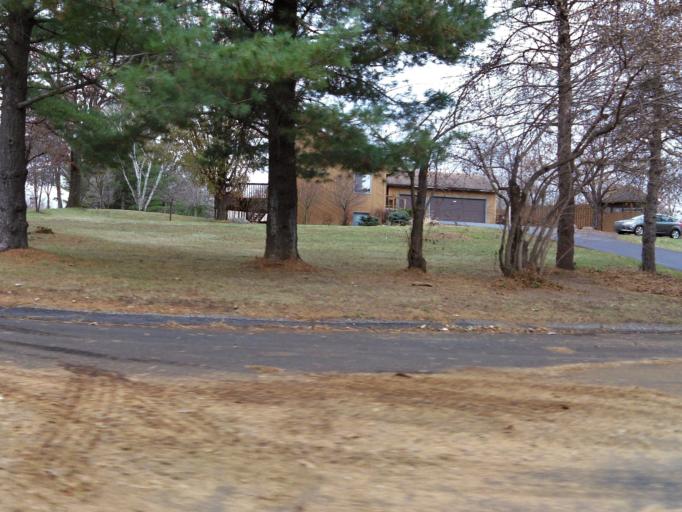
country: US
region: Minnesota
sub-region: Washington County
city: Lake Elmo
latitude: 44.9847
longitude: -92.8688
